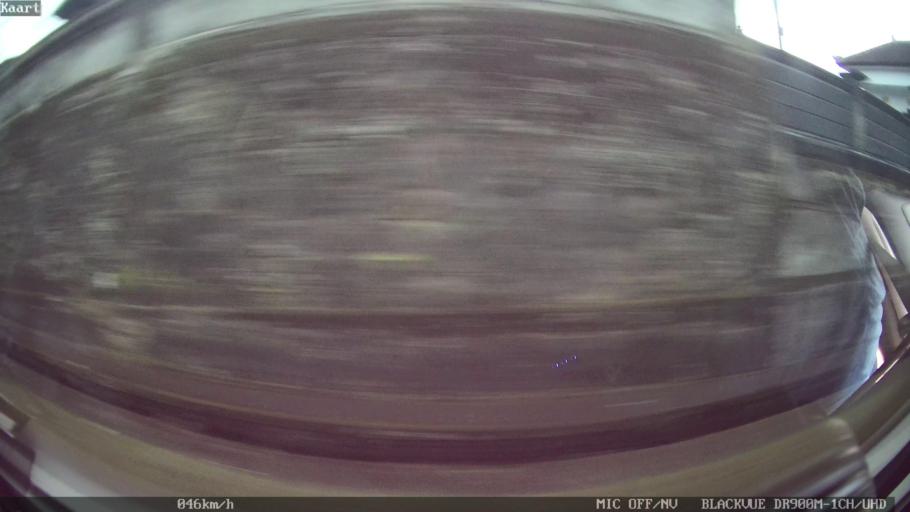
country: ID
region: Bali
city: Empalan
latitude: -8.3974
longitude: 115.1504
